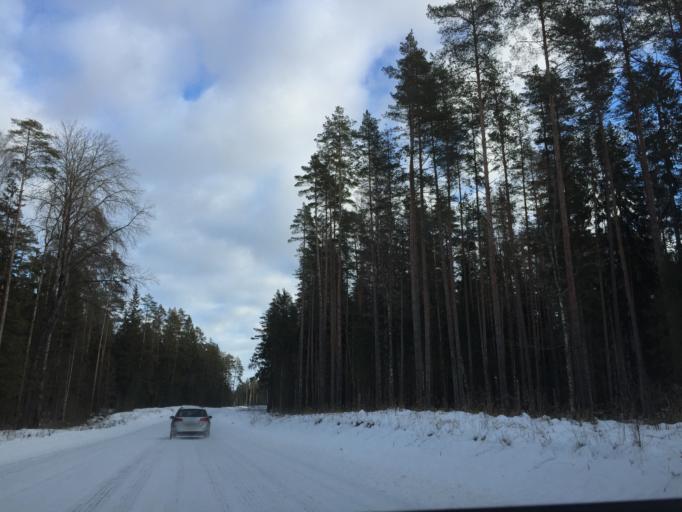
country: LV
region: Ogre
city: Jumprava
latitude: 56.5479
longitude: 24.8713
